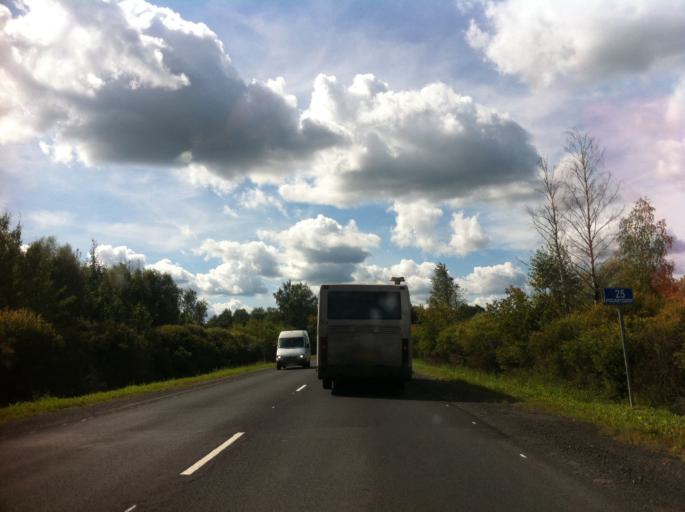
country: RU
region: Pskov
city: Izborsk
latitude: 57.7254
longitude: 27.9529
